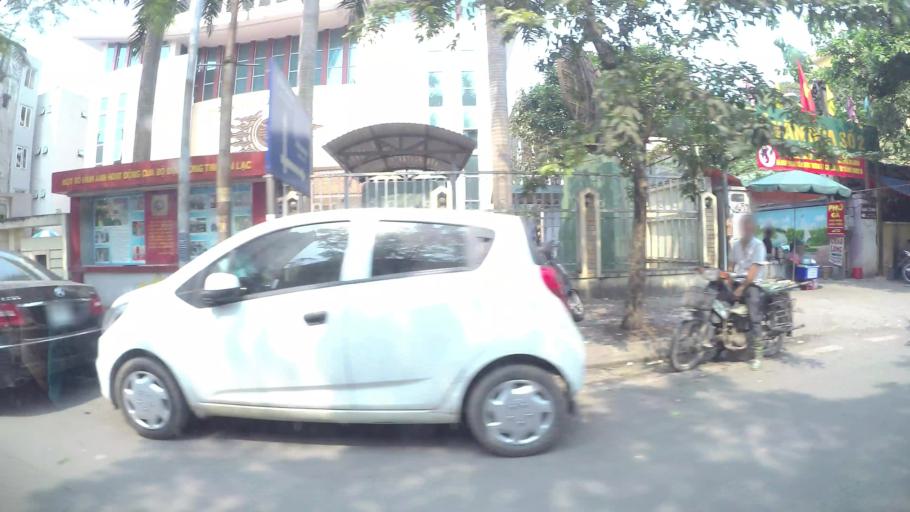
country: VN
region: Ha Noi
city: Dong Da
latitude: 21.0305
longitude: 105.8269
